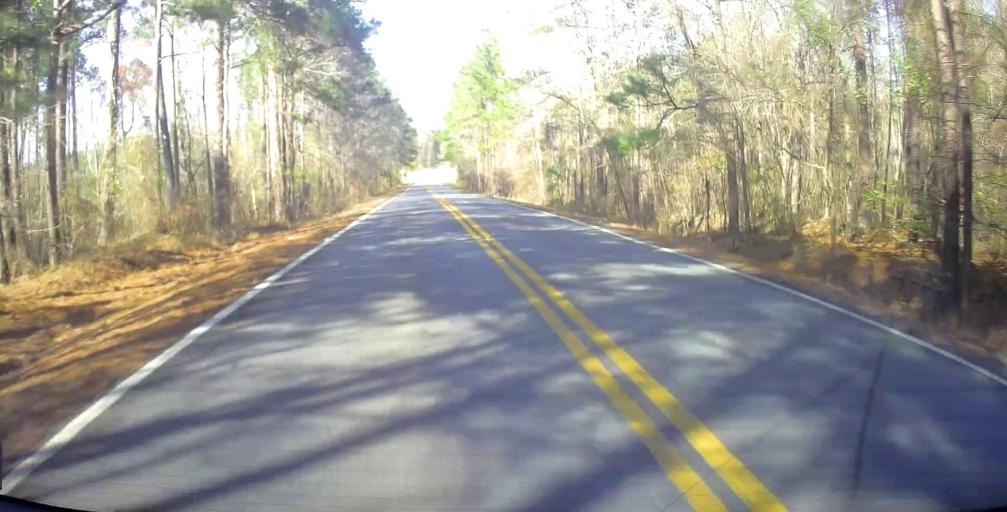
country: US
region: Georgia
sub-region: Twiggs County
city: Jeffersonville
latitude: 32.7544
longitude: -83.3435
